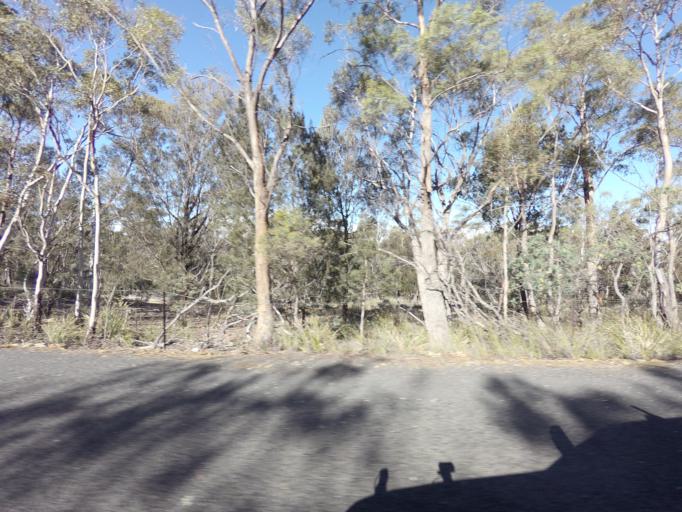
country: AU
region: Tasmania
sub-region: Sorell
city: Sorell
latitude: -42.3604
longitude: 147.9568
